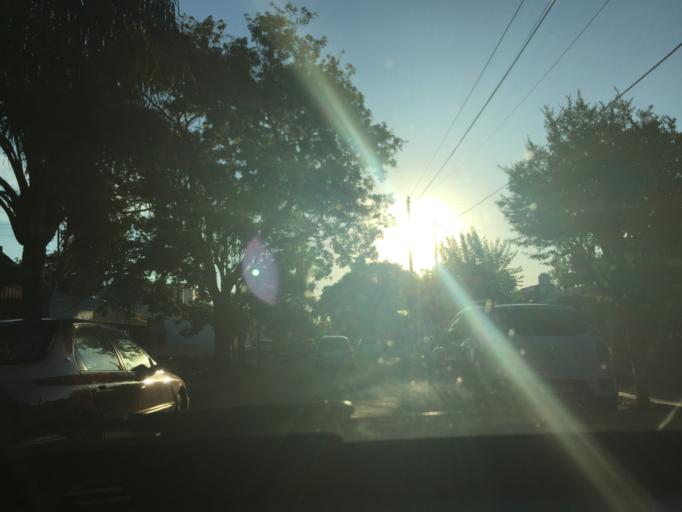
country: AR
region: Cordoba
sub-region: Departamento de Capital
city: Cordoba
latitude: -31.3670
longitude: -64.2351
